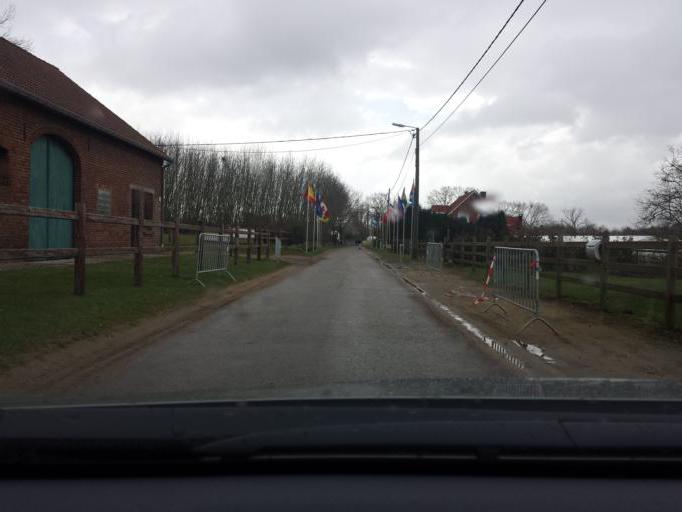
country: BE
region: Flanders
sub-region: Provincie Limburg
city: Lummen
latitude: 50.9791
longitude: 5.1575
